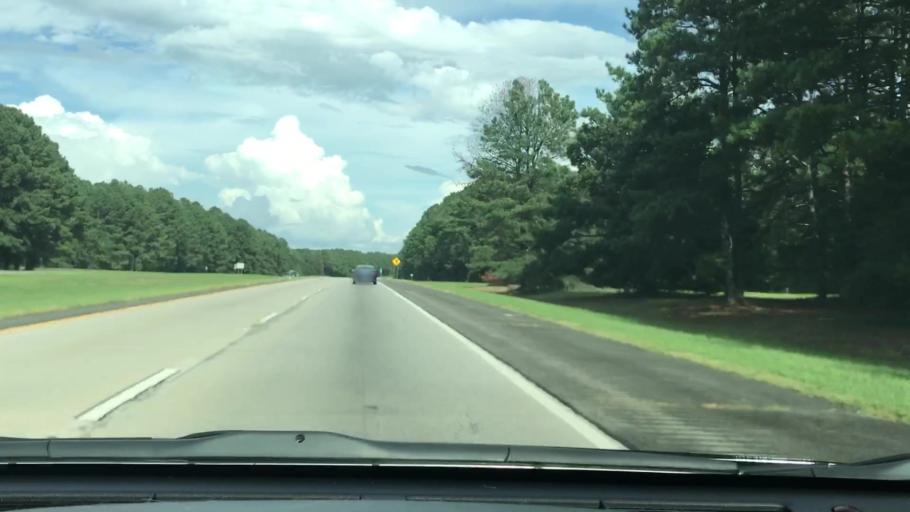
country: US
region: Georgia
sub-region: Taliaferro County
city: Crawfordville
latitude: 33.5295
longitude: -82.9096
